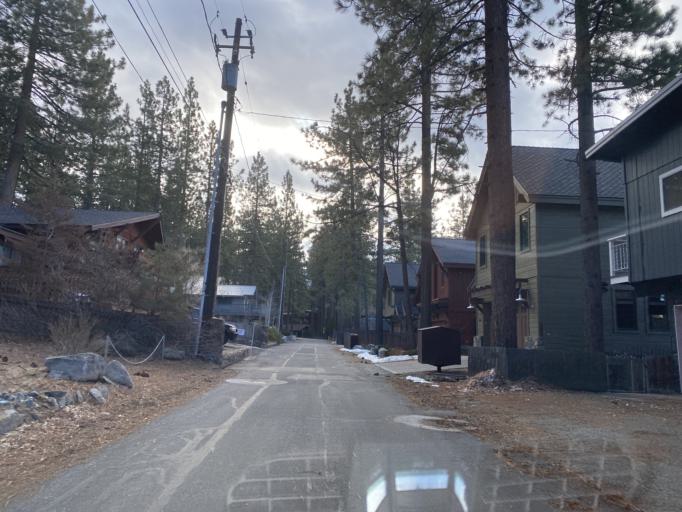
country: US
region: Nevada
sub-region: Douglas County
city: Kingsbury
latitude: 38.9982
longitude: -119.9565
